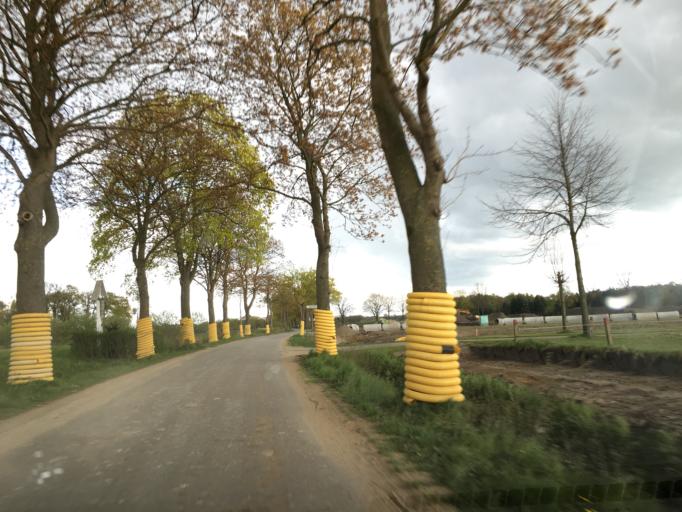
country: DE
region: North Rhine-Westphalia
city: Ludinghausen
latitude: 51.7822
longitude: 7.4624
